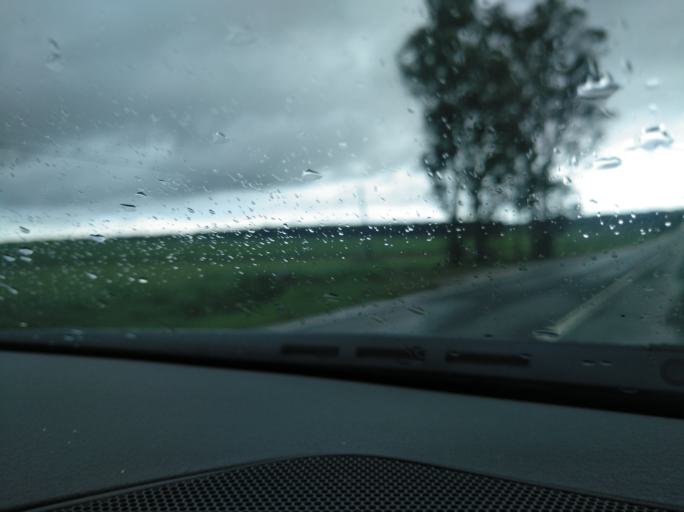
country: PT
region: Beja
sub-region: Aljustrel
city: Aljustrel
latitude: 37.8276
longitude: -8.1104
